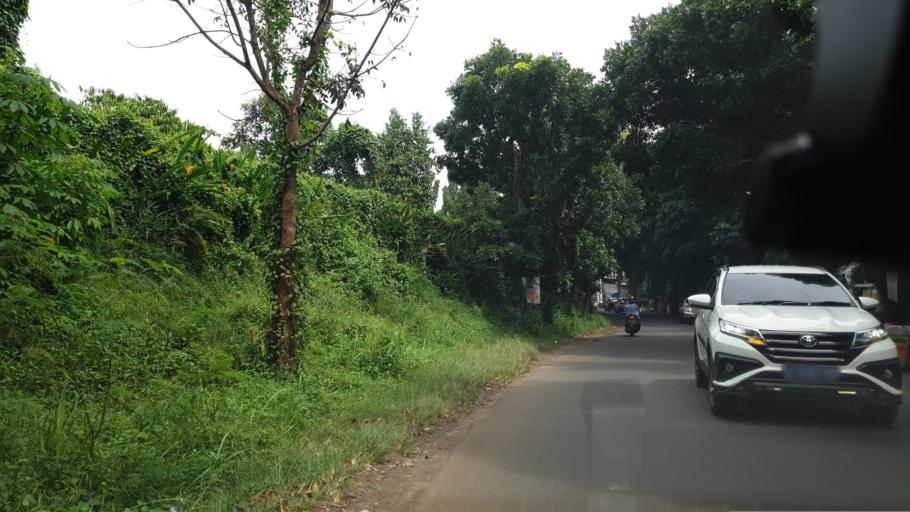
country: ID
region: West Java
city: Pamulang
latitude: -6.3487
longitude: 106.7652
